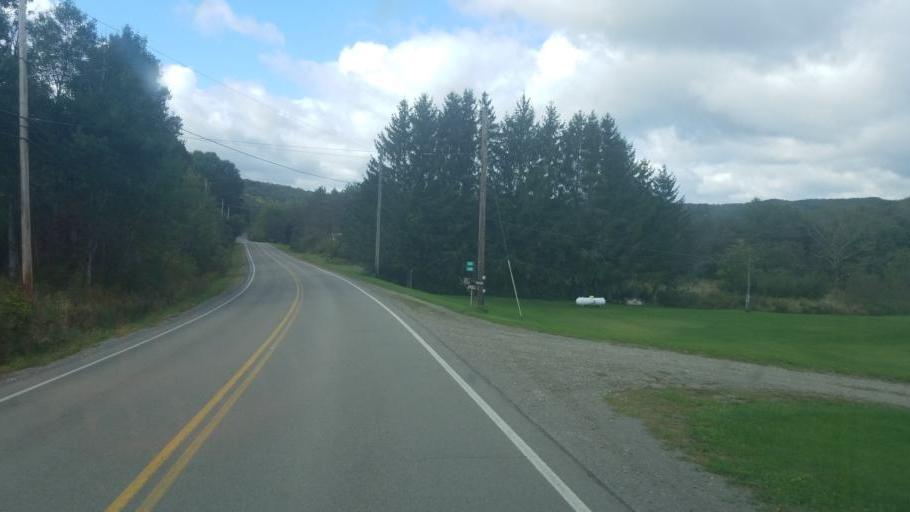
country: US
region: New York
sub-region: Allegany County
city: Cuba
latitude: 42.1481
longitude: -78.3048
